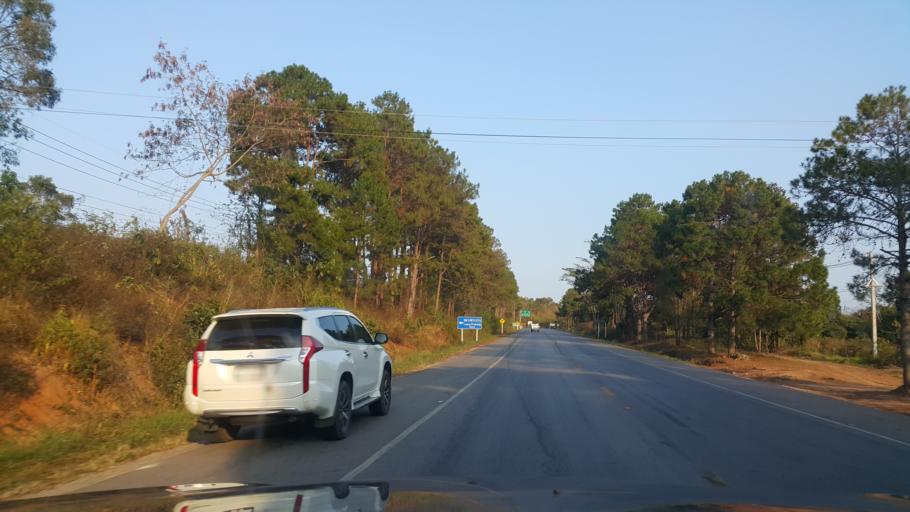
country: TH
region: Loei
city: Phu Ruea
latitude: 17.4510
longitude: 101.4809
